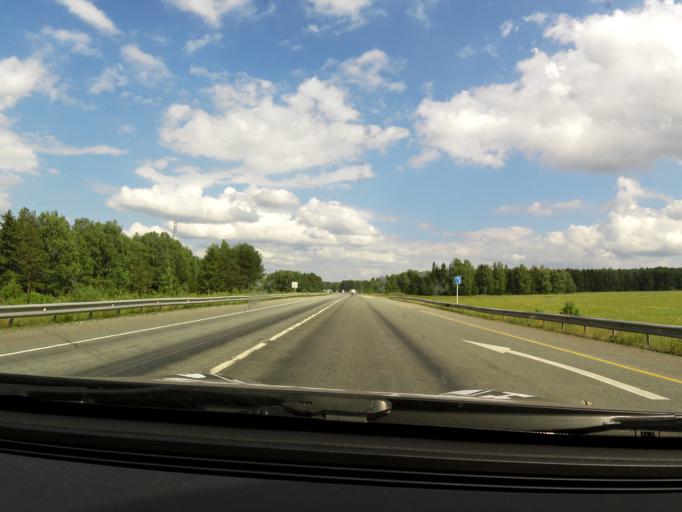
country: RU
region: Sverdlovsk
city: Bisert'
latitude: 56.8294
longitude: 59.0518
